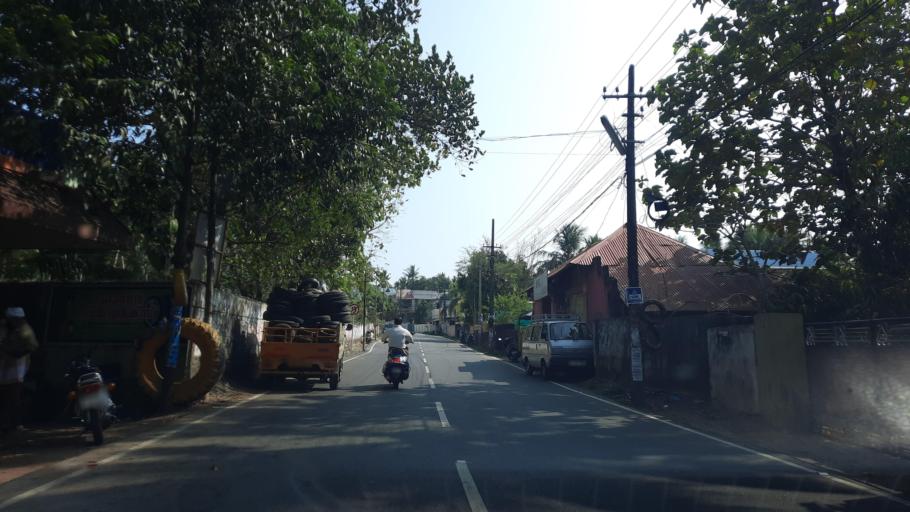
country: IN
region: Kerala
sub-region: Thiruvananthapuram
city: Thiruvananthapuram
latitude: 8.5628
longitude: 76.9209
